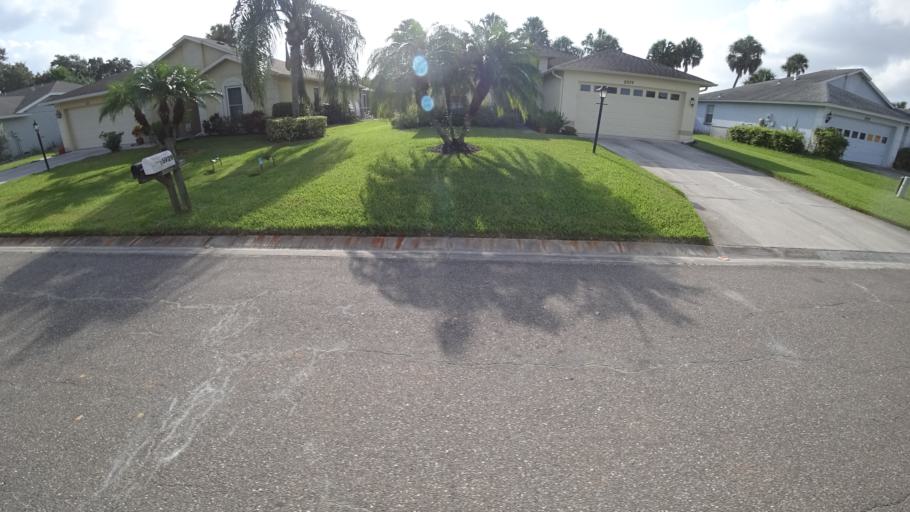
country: US
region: Florida
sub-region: Sarasota County
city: North Sarasota
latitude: 27.4169
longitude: -82.5068
